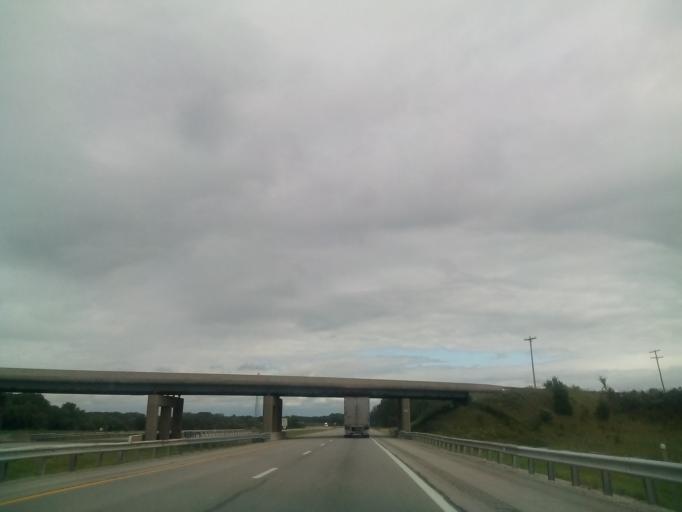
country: US
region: Ohio
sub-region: Fulton County
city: Burlington
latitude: 41.5908
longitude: -84.3531
